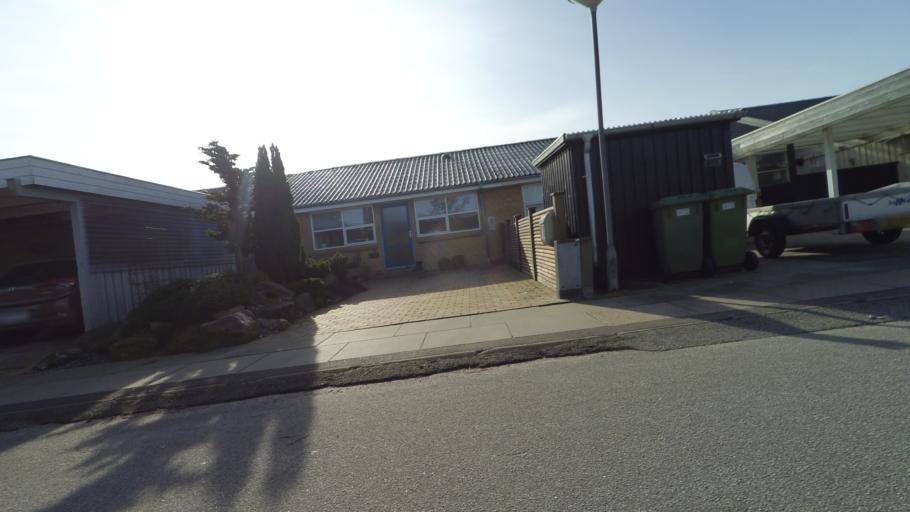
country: DK
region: Central Jutland
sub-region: Arhus Kommune
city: Tranbjerg
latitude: 56.0877
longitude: 10.1225
